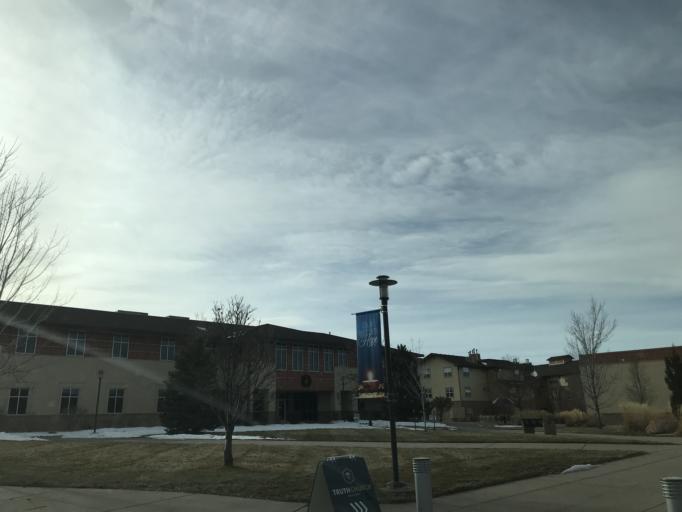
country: US
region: Colorado
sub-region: Arapahoe County
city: Columbine Valley
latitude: 39.6009
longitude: -105.0216
